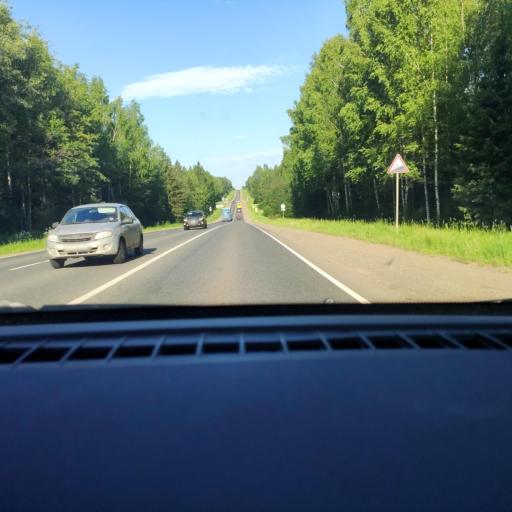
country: RU
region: Udmurtiya
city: Khokhryaki
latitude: 56.9166
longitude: 53.4466
